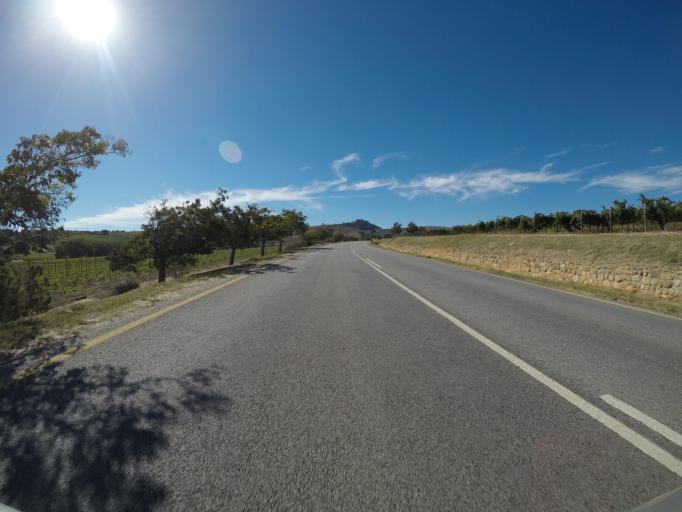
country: ZA
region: Western Cape
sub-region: City of Cape Town
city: Kraaifontein
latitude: -33.9673
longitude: 18.7452
